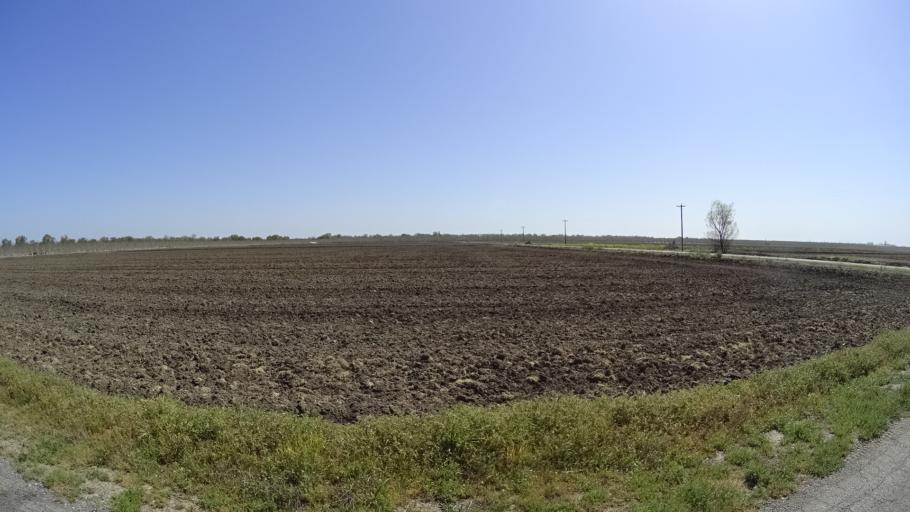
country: US
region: California
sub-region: Glenn County
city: Willows
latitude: 39.4816
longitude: -122.0375
